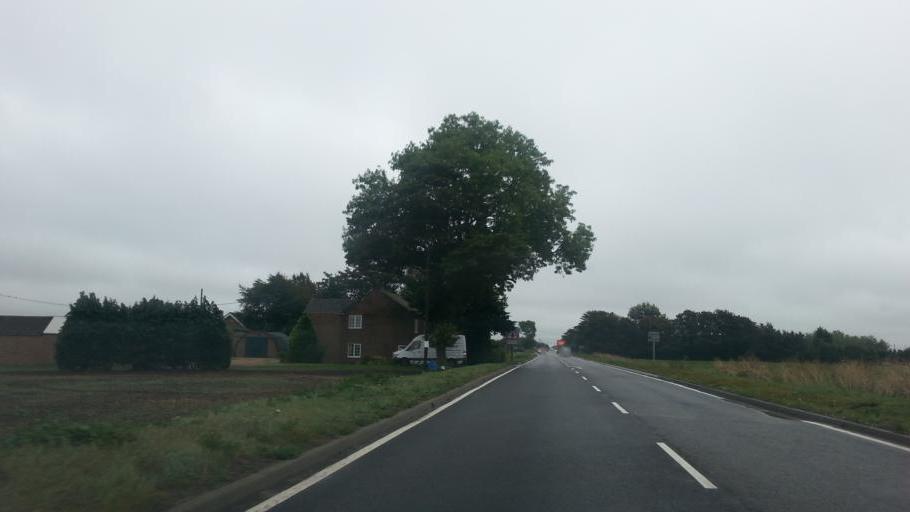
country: GB
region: England
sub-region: Peterborough
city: Thorney
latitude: 52.6149
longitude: -0.0038
